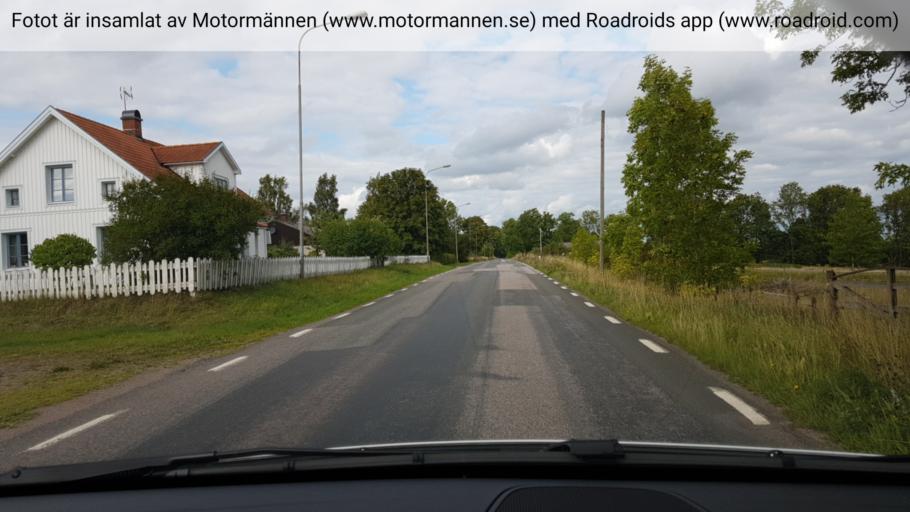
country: SE
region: Vaestra Goetaland
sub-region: Skovde Kommun
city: Skultorp
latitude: 58.2869
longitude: 13.7971
